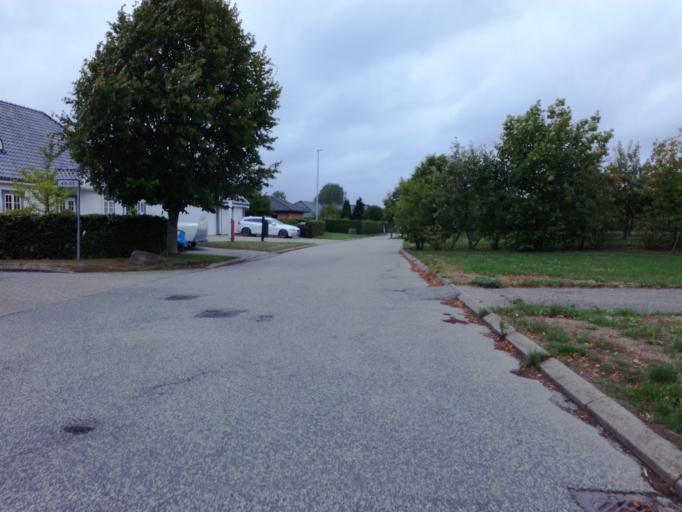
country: DK
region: South Denmark
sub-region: Vejle Kommune
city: Borkop
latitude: 55.6373
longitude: 9.6439
